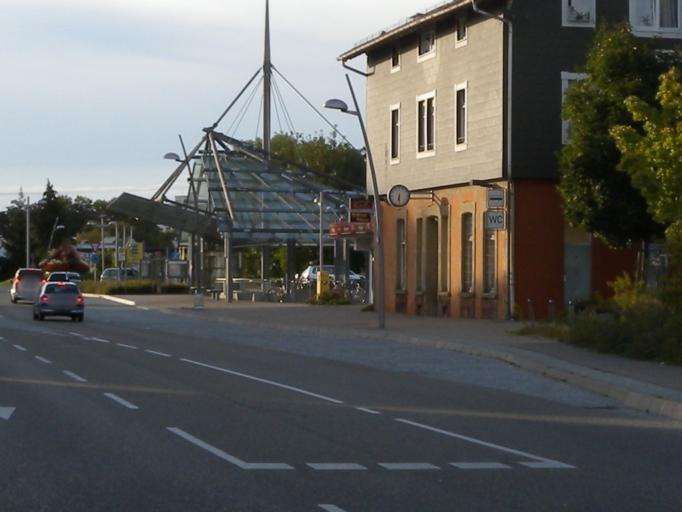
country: DE
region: Baden-Wuerttemberg
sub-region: Regierungsbezirk Stuttgart
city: Tamm
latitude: 48.9214
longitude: 9.1257
